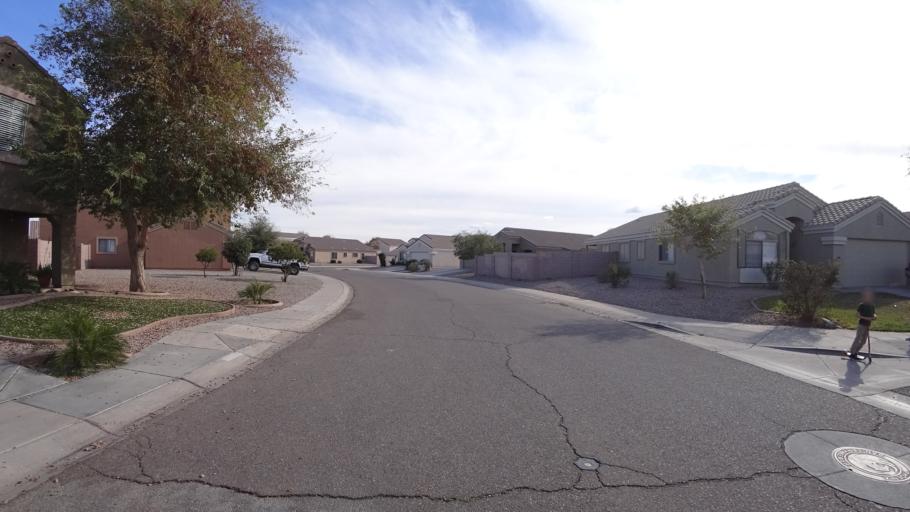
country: US
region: Arizona
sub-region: Maricopa County
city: Tolleson
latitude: 33.4262
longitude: -112.2883
